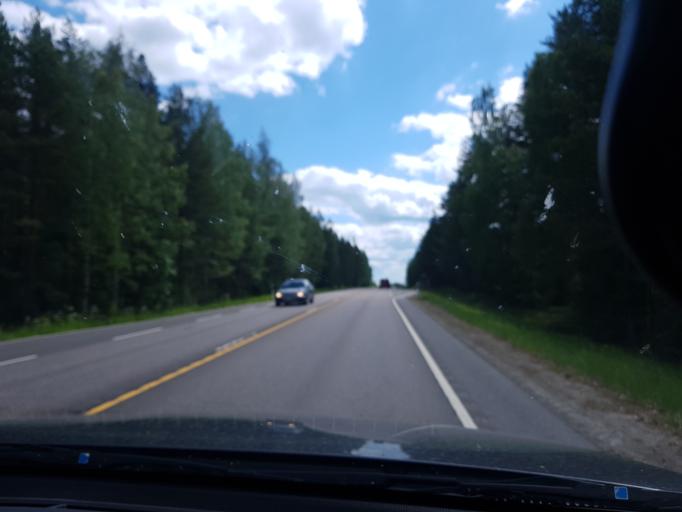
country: FI
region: Haeme
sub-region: Haemeenlinna
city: Parola
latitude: 61.1346
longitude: 24.4172
